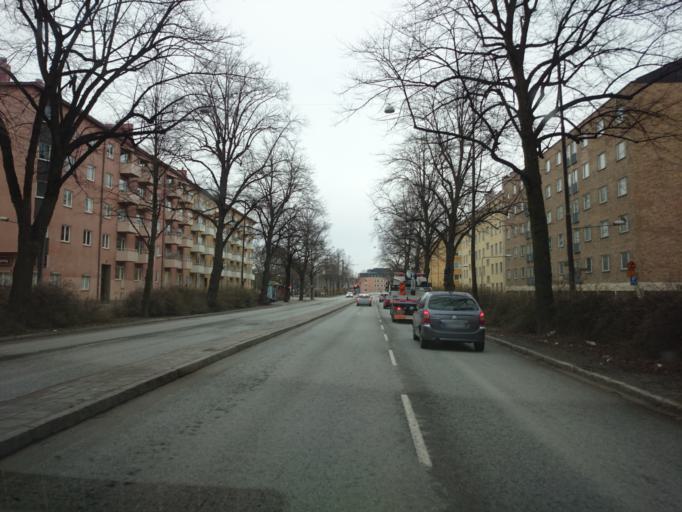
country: SE
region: Uppsala
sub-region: Uppsala Kommun
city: Uppsala
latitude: 59.8634
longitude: 17.6251
